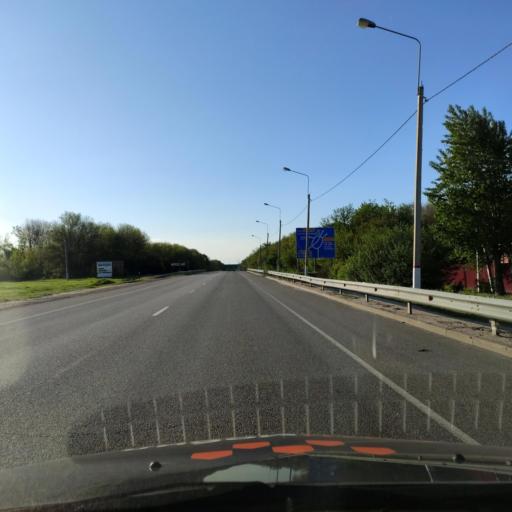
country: RU
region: Lipetsk
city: Yelets
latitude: 52.5511
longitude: 38.7084
